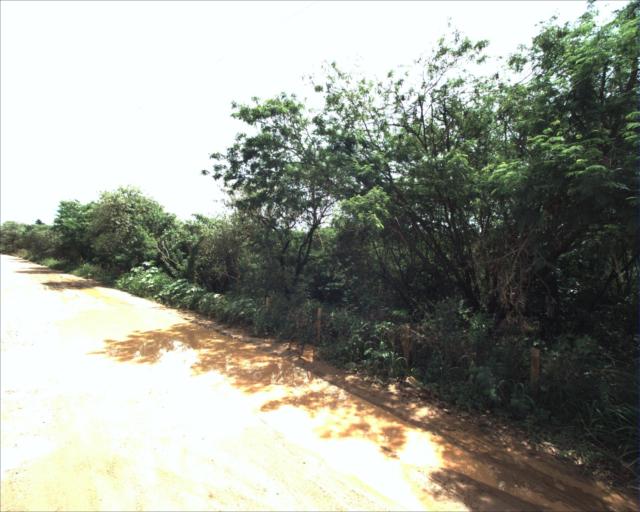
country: BR
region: Sao Paulo
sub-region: Aracoiaba Da Serra
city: Aracoiaba da Serra
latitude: -23.5570
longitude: -47.5538
